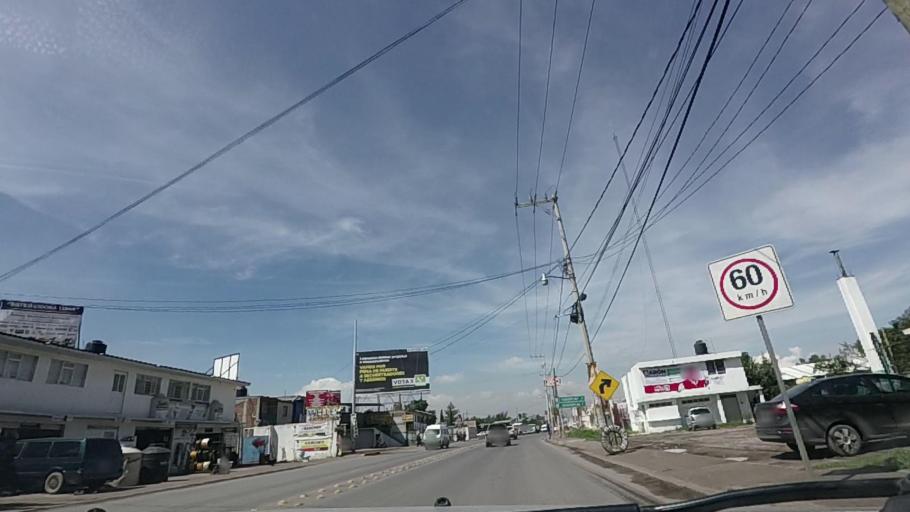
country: MX
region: Mexico
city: Teoloyucan
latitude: 19.7378
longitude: -99.1818
